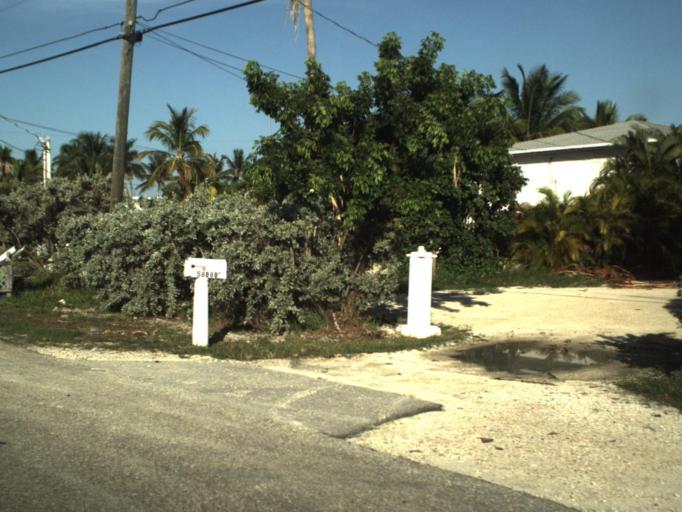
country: US
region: Florida
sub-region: Monroe County
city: Marathon
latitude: 24.7589
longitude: -80.9556
